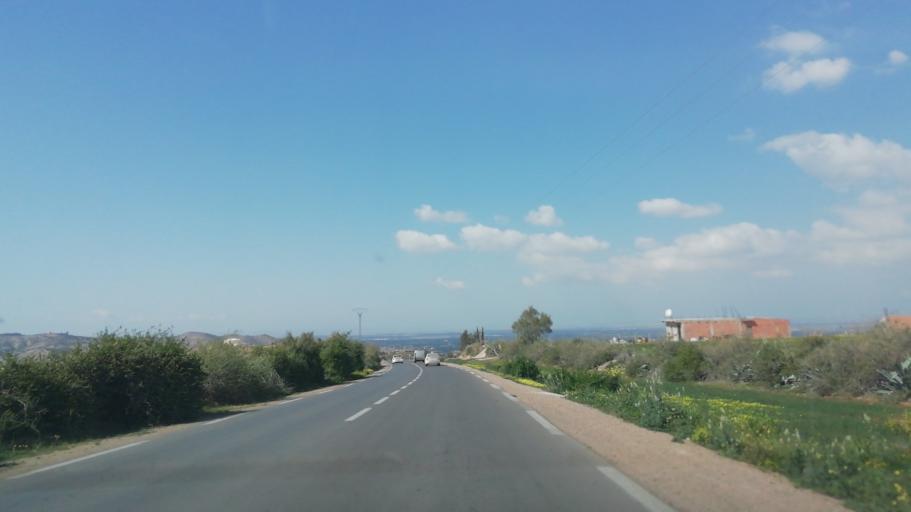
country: DZ
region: Mascara
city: Mascara
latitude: 35.5522
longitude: 0.0833
